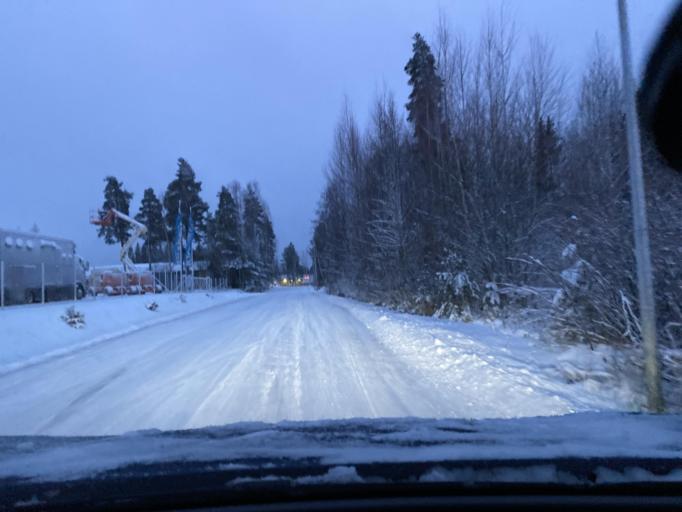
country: FI
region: Pirkanmaa
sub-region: Lounais-Pirkanmaa
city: Vammala
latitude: 61.3099
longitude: 22.9316
